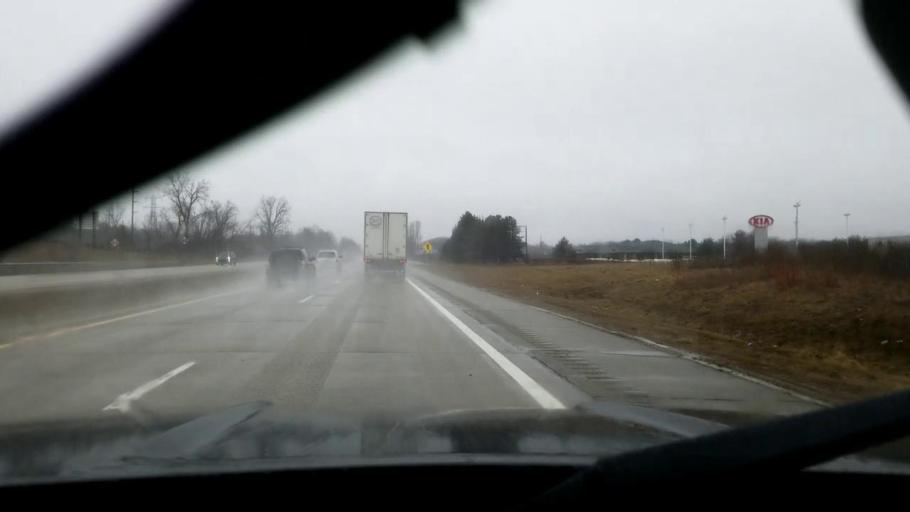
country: US
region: Michigan
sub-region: Jackson County
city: Michigan Center
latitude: 42.2399
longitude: -84.3557
